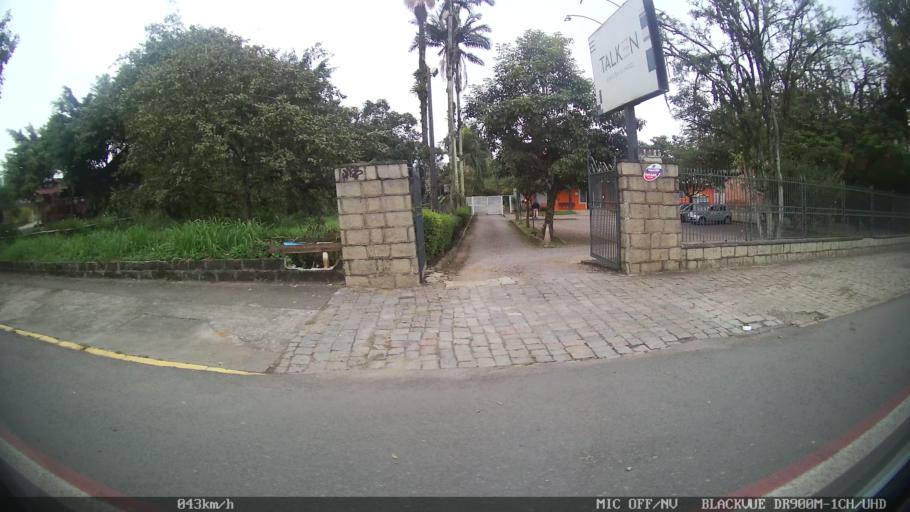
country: BR
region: Santa Catarina
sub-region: Joinville
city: Joinville
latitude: -26.2890
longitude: -48.8406
